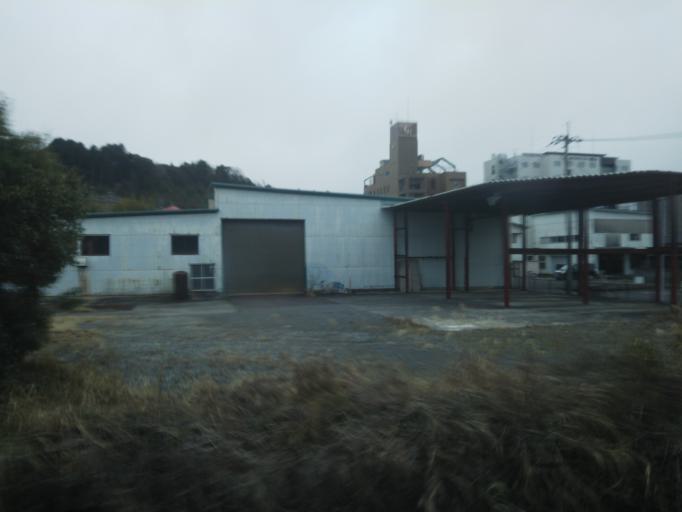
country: JP
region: Kochi
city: Nakamura
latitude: 32.9816
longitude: 132.9465
